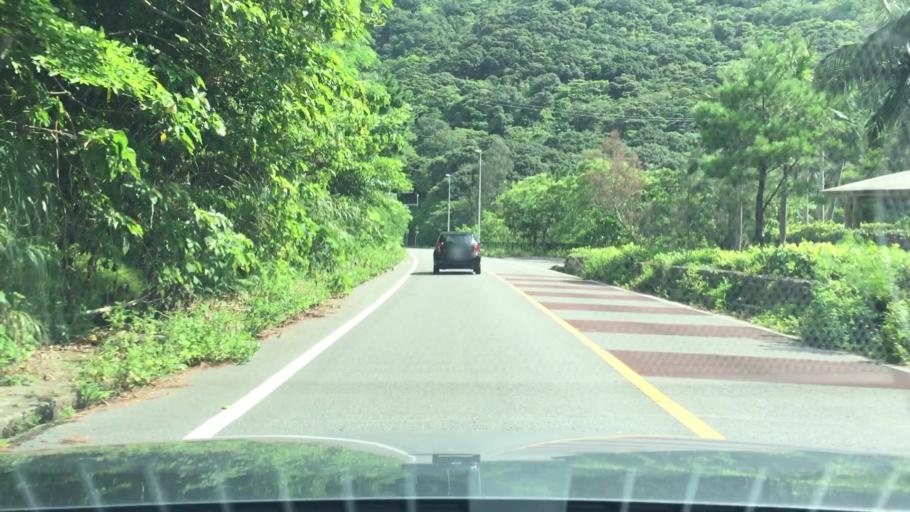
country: JP
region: Okinawa
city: Ishigaki
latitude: 24.4359
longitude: 124.2118
